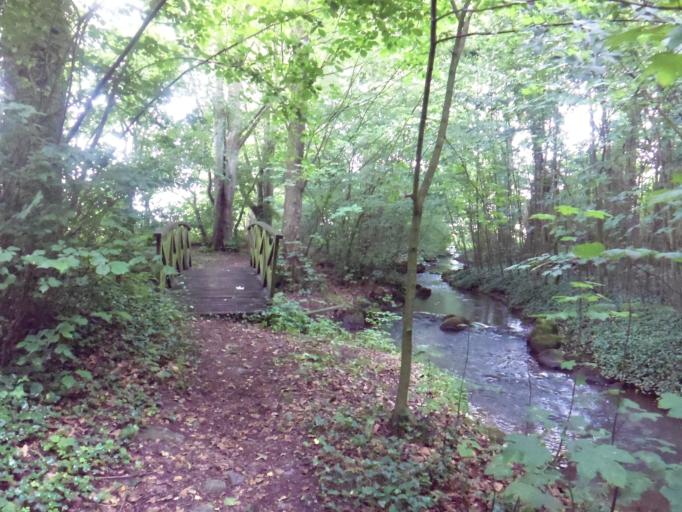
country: DK
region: South Denmark
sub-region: Tonder Kommune
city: Toftlund
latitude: 55.1162
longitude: 9.0756
